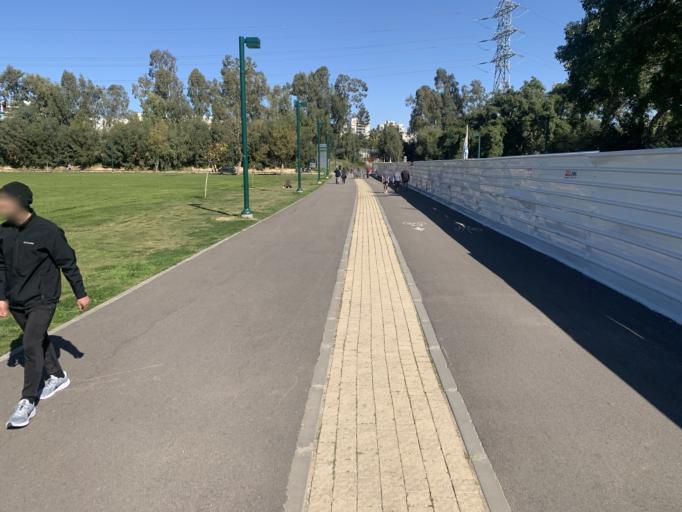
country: IL
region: Tel Aviv
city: Ramat Gan
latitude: 32.1025
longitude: 34.8196
